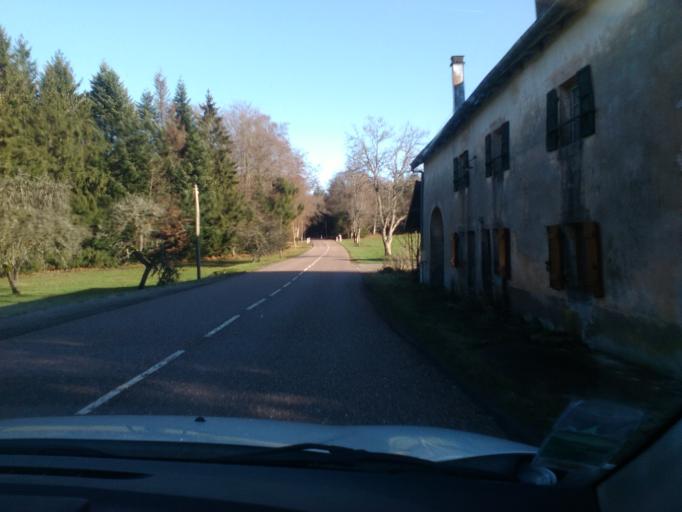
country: FR
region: Lorraine
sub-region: Departement des Vosges
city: Remiremont
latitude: 47.9777
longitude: 6.5426
